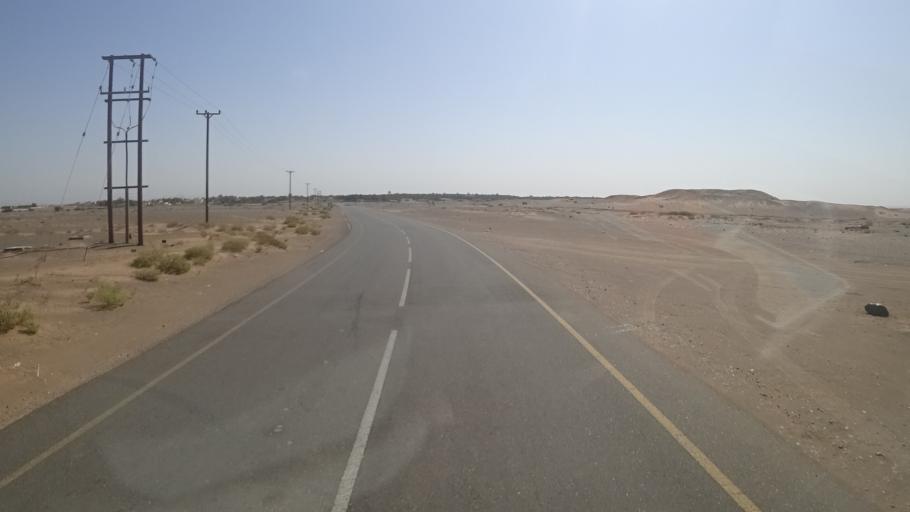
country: OM
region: Ash Sharqiyah
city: Al Qabil
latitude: 22.4977
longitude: 58.7313
